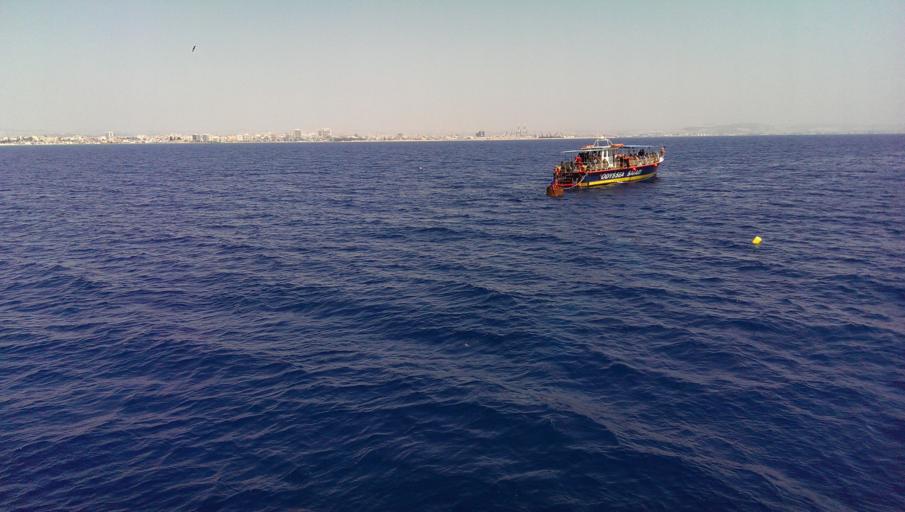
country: CY
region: Larnaka
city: Larnaca
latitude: 34.8968
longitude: 33.6577
